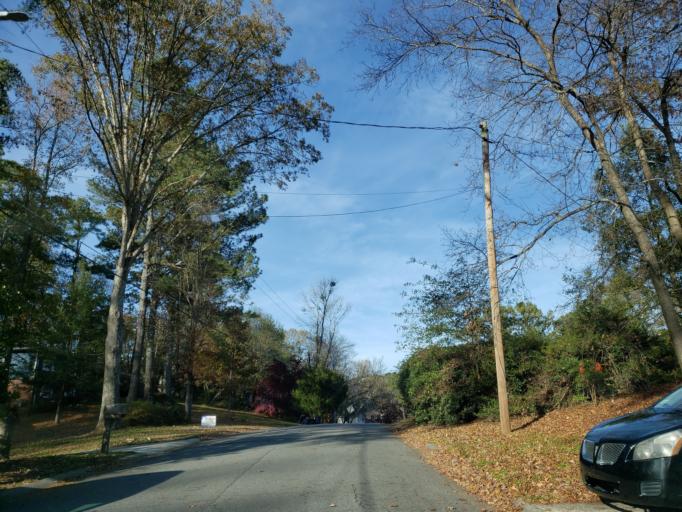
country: US
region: Georgia
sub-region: Cobb County
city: Kennesaw
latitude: 34.0265
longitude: -84.6070
